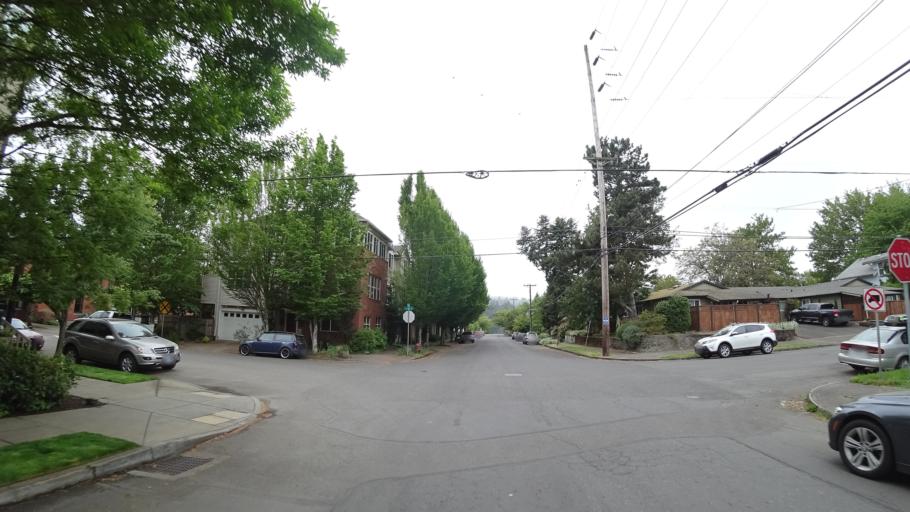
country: US
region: Oregon
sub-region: Clackamas County
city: Milwaukie
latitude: 45.4593
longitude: -122.6548
